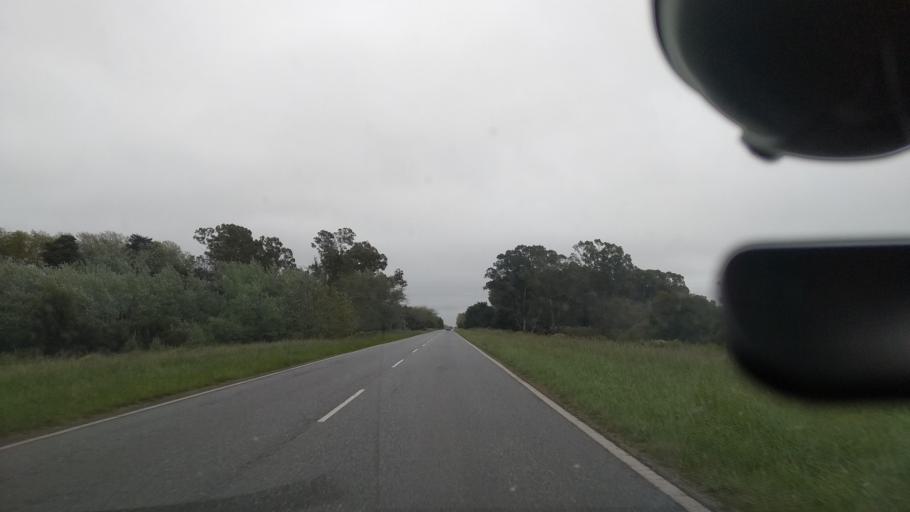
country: AR
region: Buenos Aires
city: Veronica
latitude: -35.3107
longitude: -57.4906
